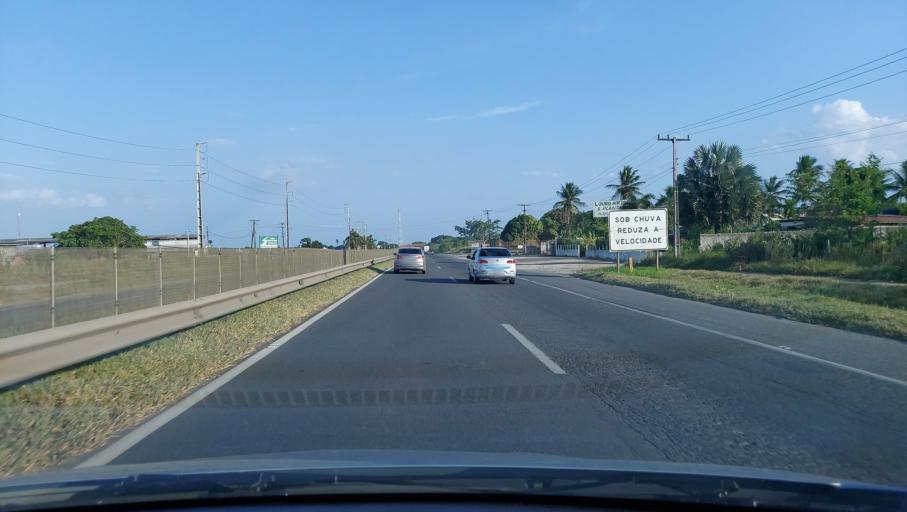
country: BR
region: Bahia
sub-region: Conceicao Do Jacuipe
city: Conceicao do Jacuipe
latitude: -12.3834
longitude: -38.7950
